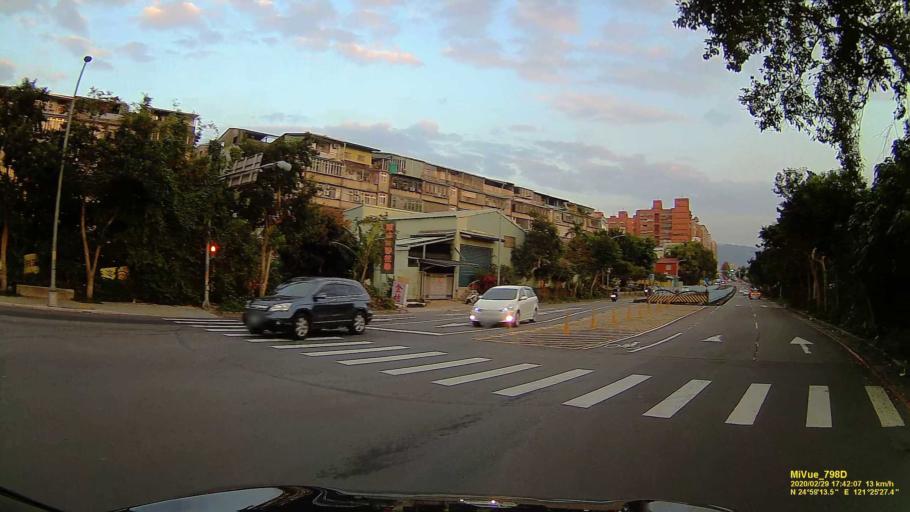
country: TW
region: Taipei
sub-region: Taipei
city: Banqiao
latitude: 24.9867
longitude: 121.4245
